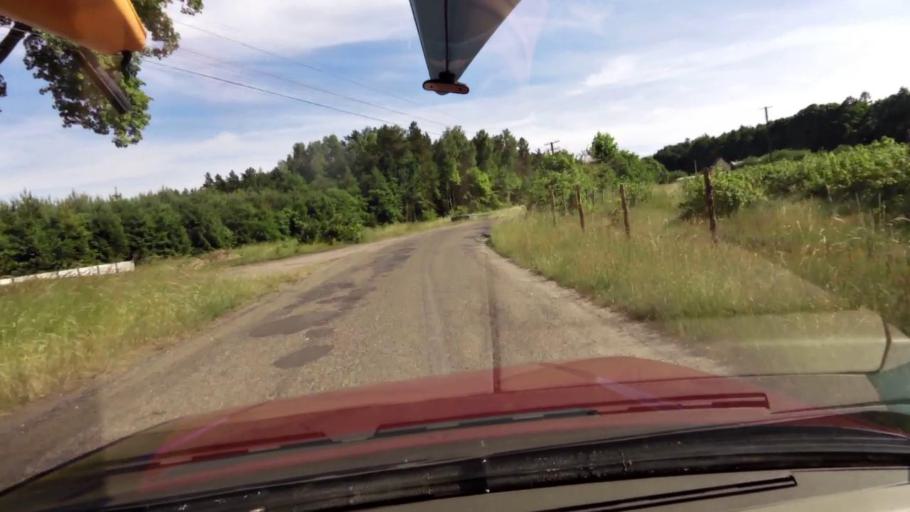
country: PL
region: Pomeranian Voivodeship
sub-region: Powiat slupski
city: Kepice
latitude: 54.1721
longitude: 16.8872
